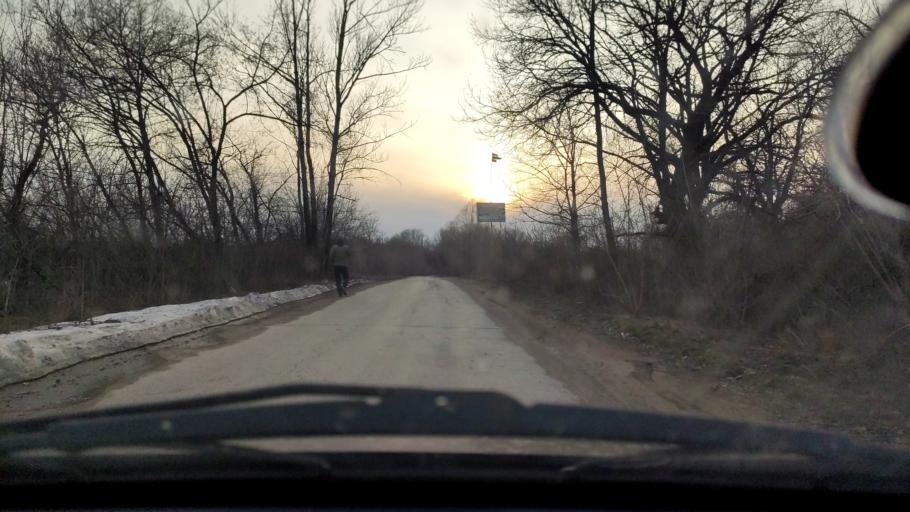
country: RU
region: Bashkortostan
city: Ufa
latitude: 54.7978
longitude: 56.1823
